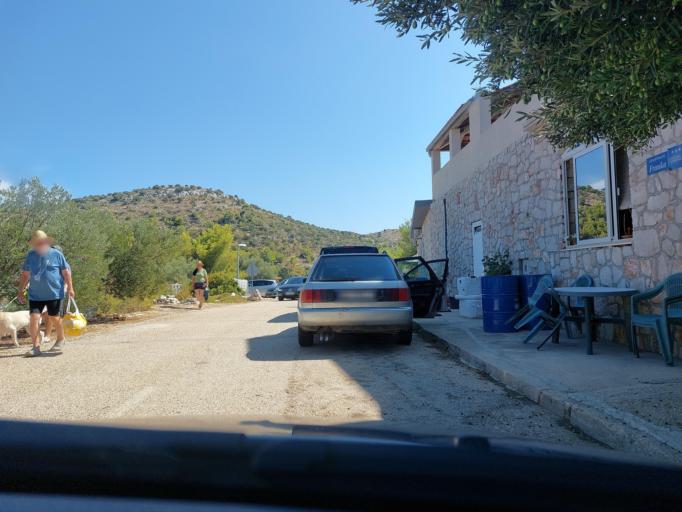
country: HR
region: Dubrovacko-Neretvanska
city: Smokvica
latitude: 42.7312
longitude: 16.8858
